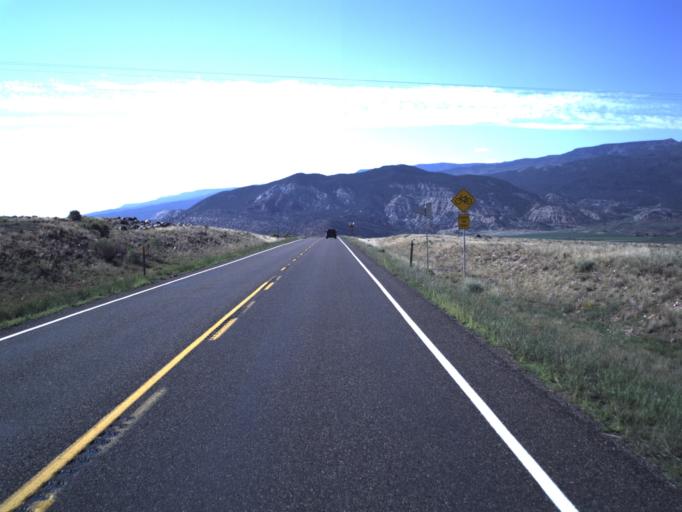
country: US
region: Utah
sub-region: Wayne County
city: Loa
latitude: 38.3327
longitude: -111.5359
